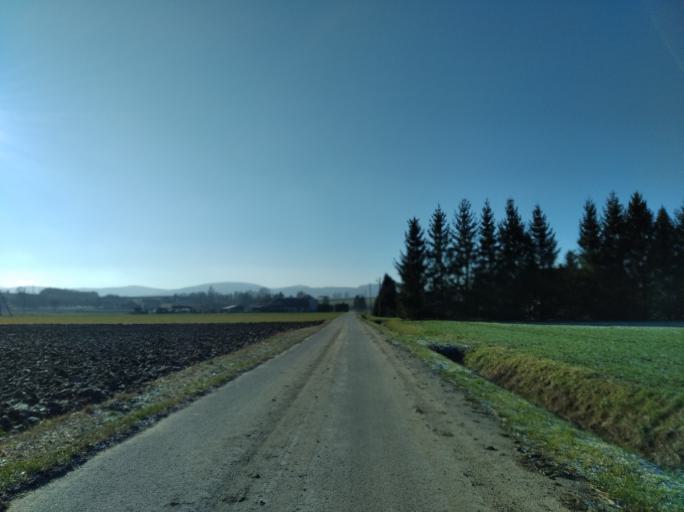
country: PL
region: Subcarpathian Voivodeship
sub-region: Powiat strzyzowski
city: Wysoka Strzyzowska
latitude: 49.8717
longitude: 21.7201
